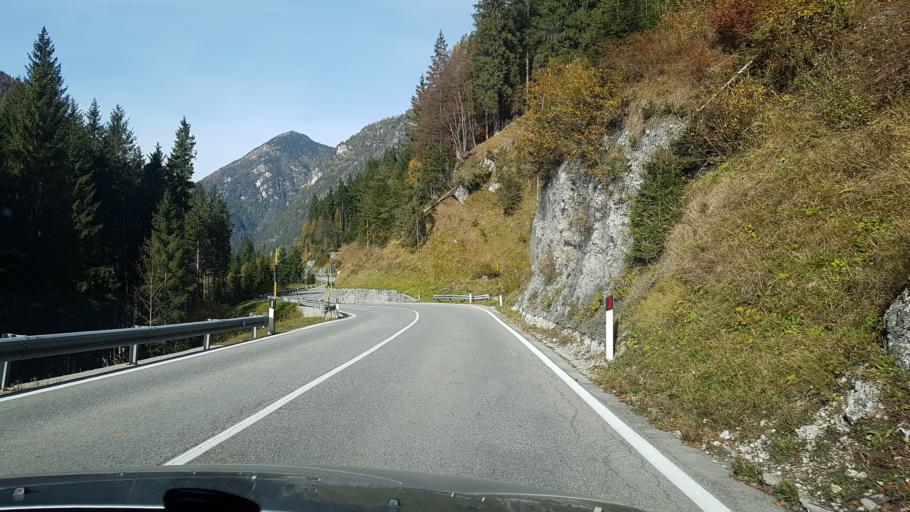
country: IT
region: Veneto
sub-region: Provincia di Belluno
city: Sappada
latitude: 46.5668
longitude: 12.6615
